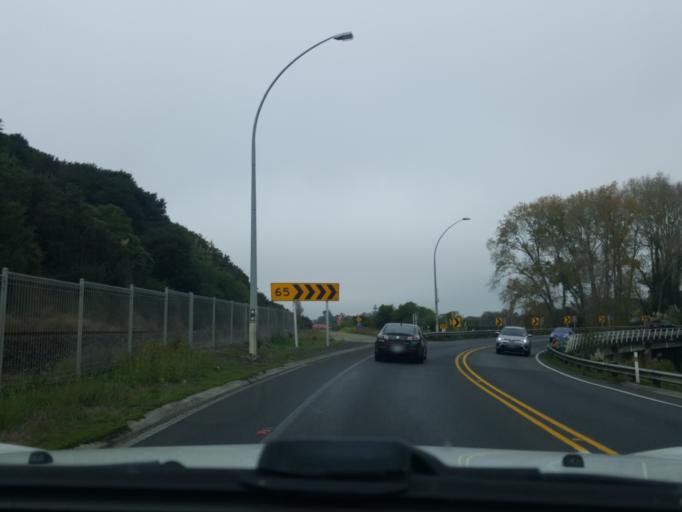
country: NZ
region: Waikato
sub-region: Waikato District
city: Ngaruawahia
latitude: -37.6084
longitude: 175.1842
